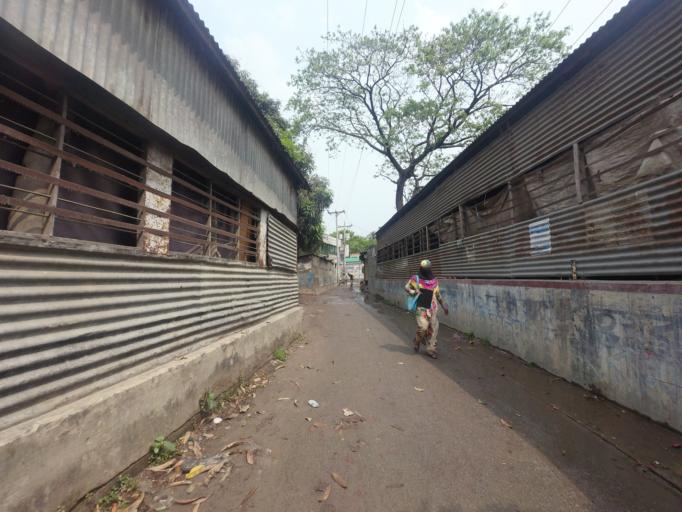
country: BD
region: Rajshahi
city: Sirajganj
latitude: 24.3269
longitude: 89.6891
